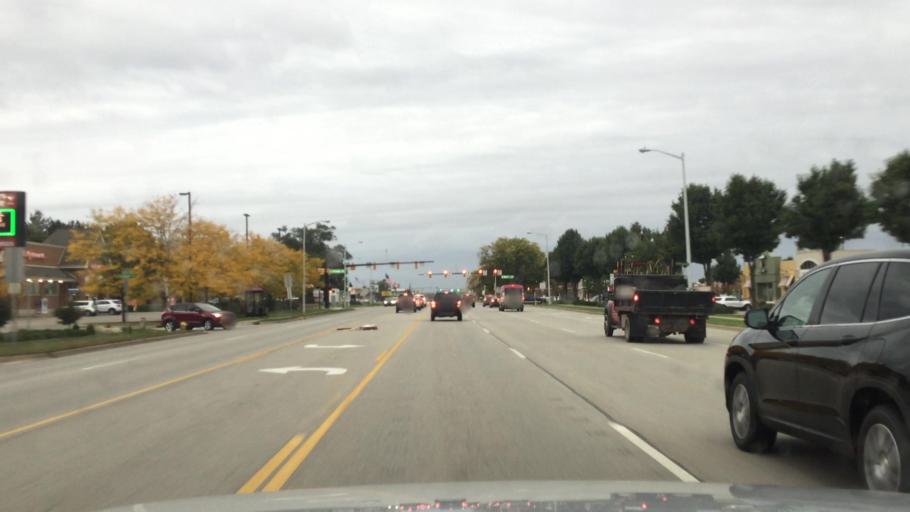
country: US
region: Michigan
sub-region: Kalamazoo County
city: Portage
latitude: 42.2315
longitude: -85.5895
